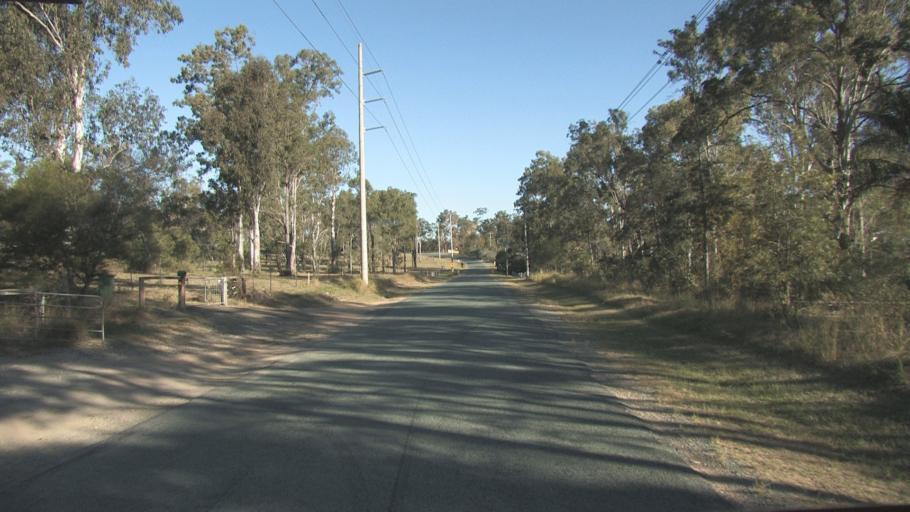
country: AU
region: Queensland
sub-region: Logan
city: North Maclean
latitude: -27.8015
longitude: 153.0410
